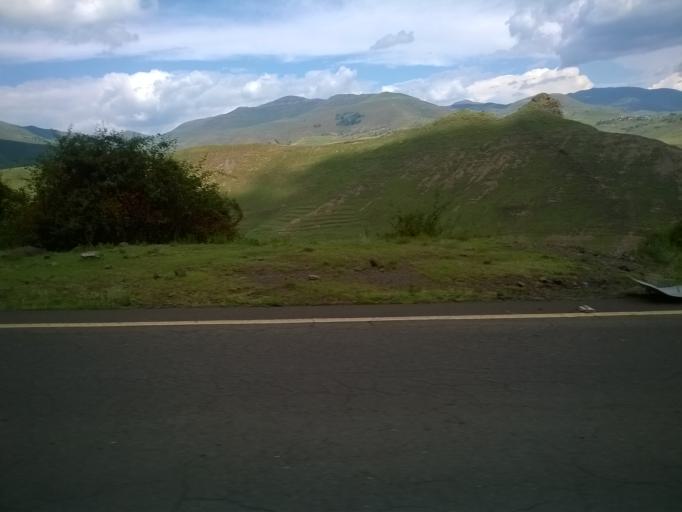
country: LS
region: Thaba-Tseka
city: Thaba-Tseka
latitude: -29.1590
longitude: 28.4837
